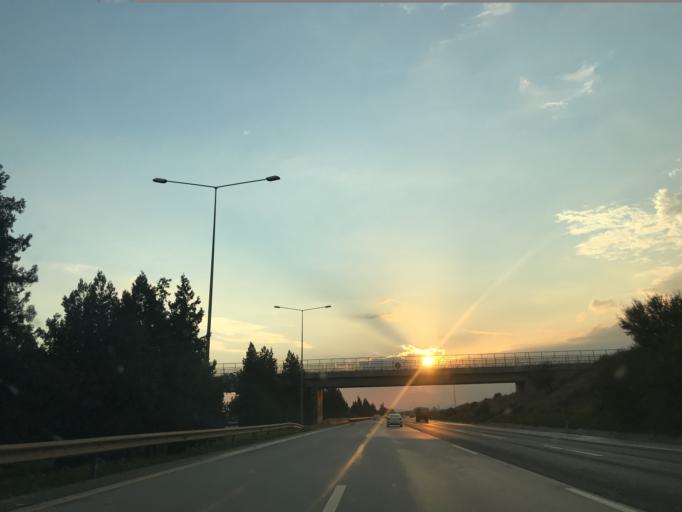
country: TR
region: Mersin
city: Yenice
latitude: 37.0261
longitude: 35.1072
